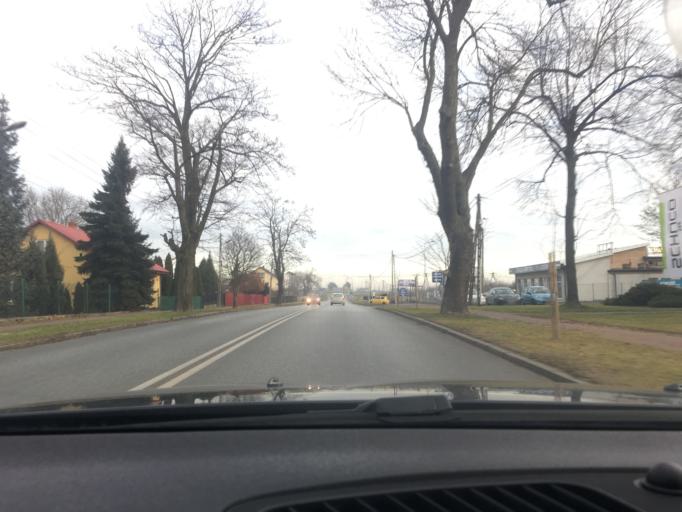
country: PL
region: Swietokrzyskie
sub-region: Powiat jedrzejowski
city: Jedrzejow
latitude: 50.6441
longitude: 20.3111
